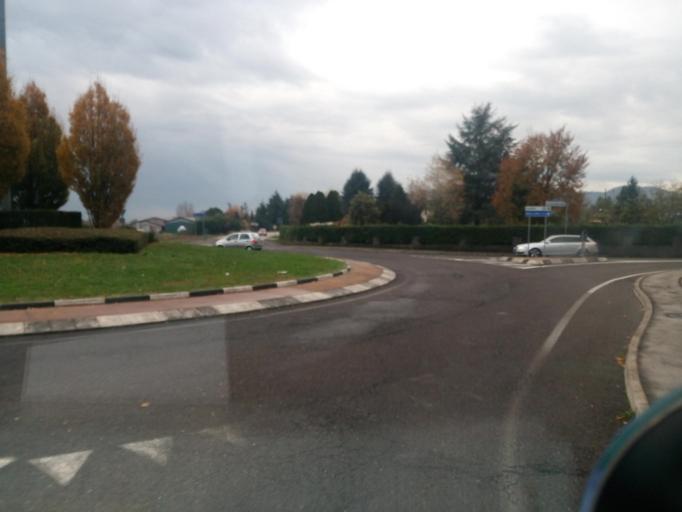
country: IT
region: Veneto
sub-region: Provincia di Vicenza
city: San Vito di Leguzzano
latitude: 45.6829
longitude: 11.3829
